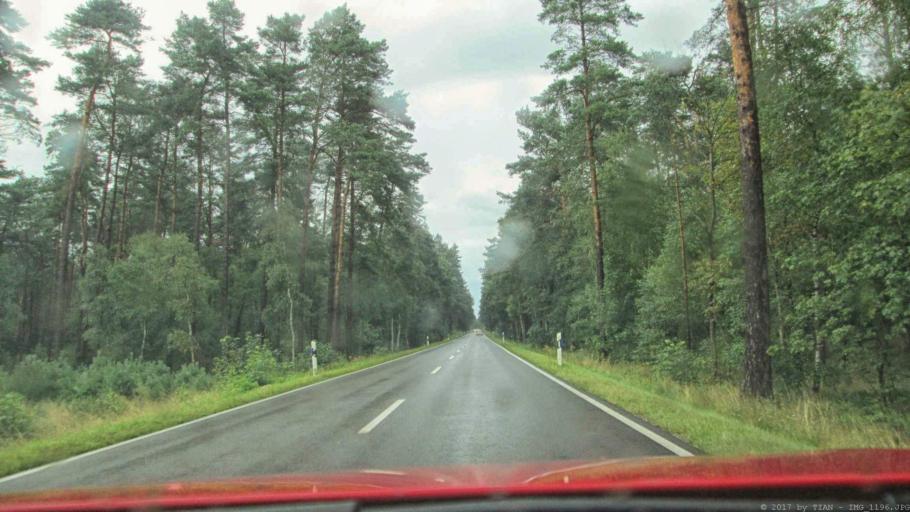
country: DE
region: Lower Saxony
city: Bergfeld
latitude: 52.6048
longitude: 10.8039
